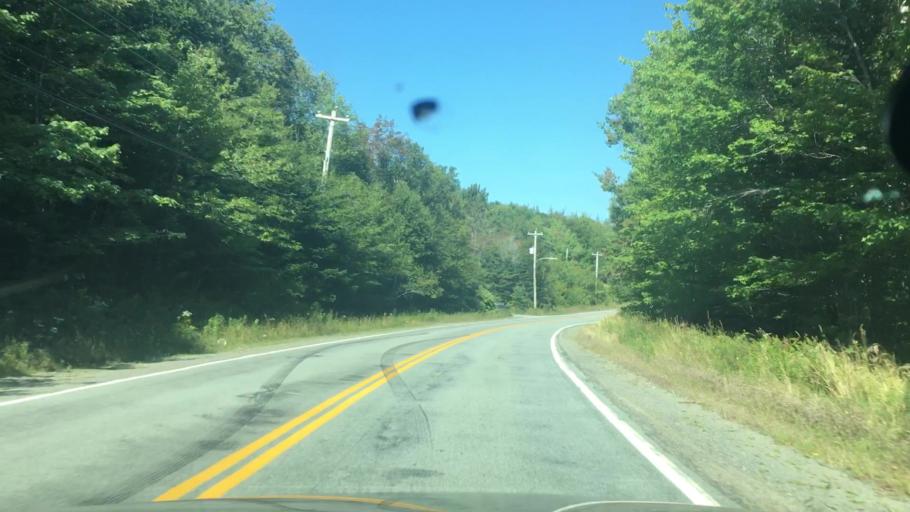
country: CA
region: Nova Scotia
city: New Glasgow
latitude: 44.9185
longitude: -62.5422
